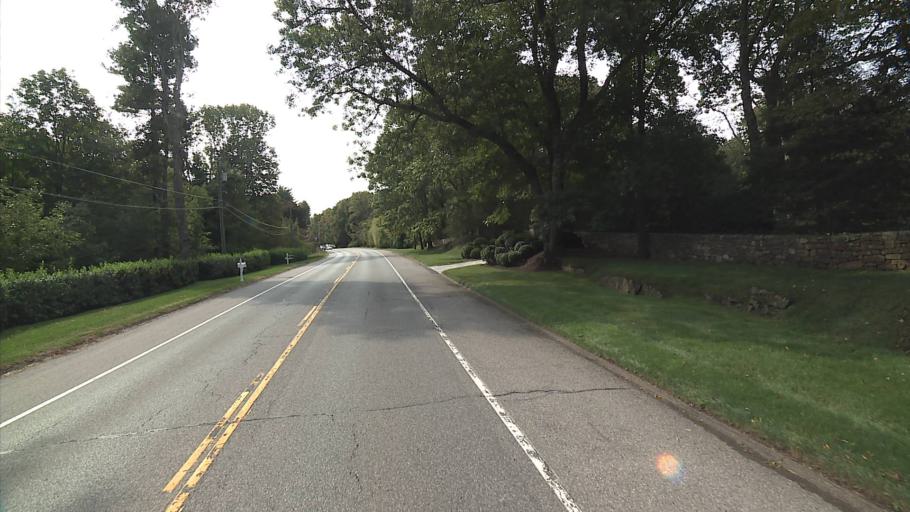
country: US
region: Connecticut
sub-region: Fairfield County
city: New Canaan
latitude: 41.1884
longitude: -73.5055
